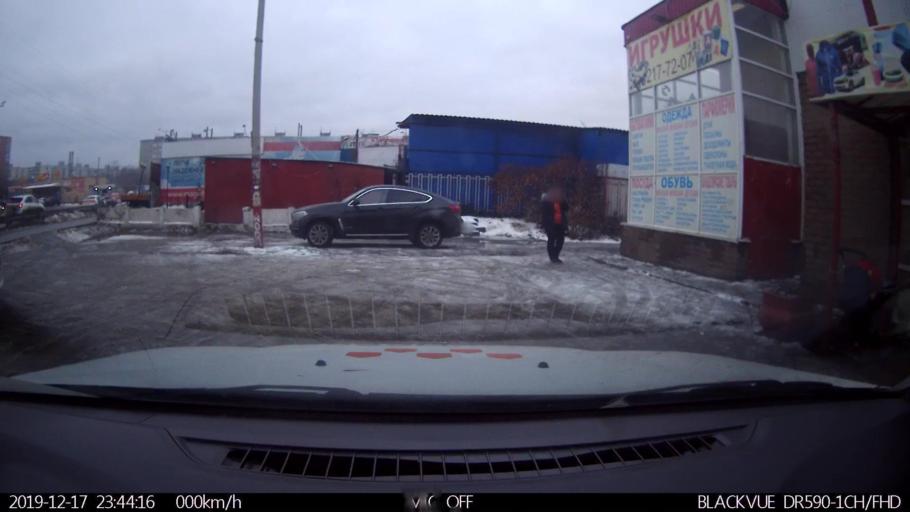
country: RU
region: Nizjnij Novgorod
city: Gorbatovka
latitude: 56.3592
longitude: 43.8268
